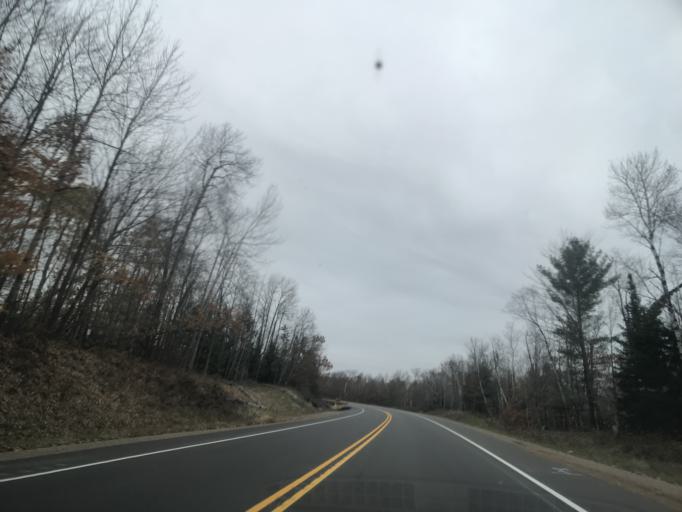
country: US
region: Wisconsin
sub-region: Menominee County
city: Legend Lake
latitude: 45.2705
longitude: -88.5091
